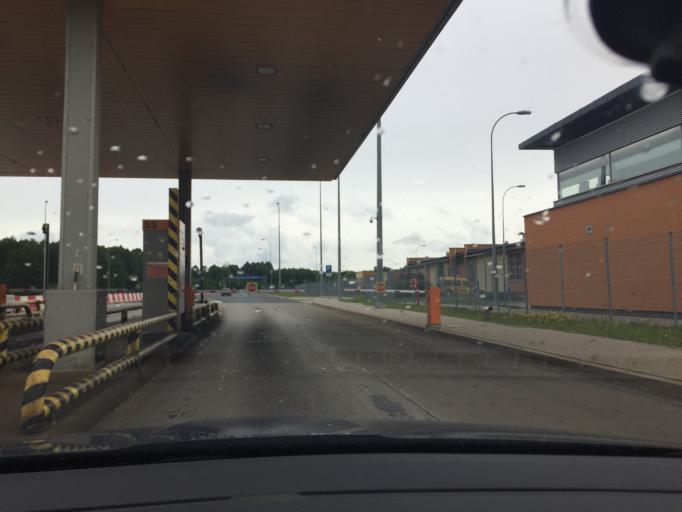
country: PL
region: Kujawsko-Pomorskie
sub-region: Powiat swiecki
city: Warlubie
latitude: 53.4680
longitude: 18.6150
